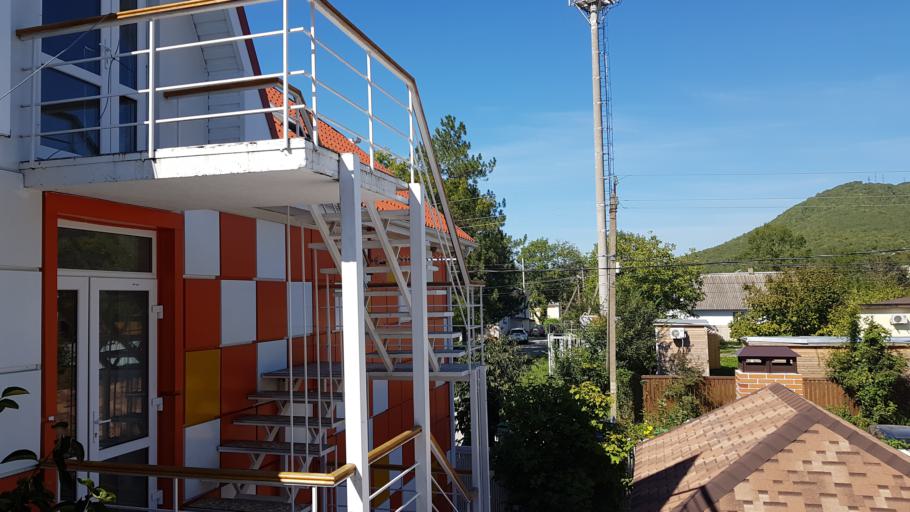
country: RU
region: Krasnodarskiy
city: Pshada
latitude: 44.4203
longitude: 38.3604
